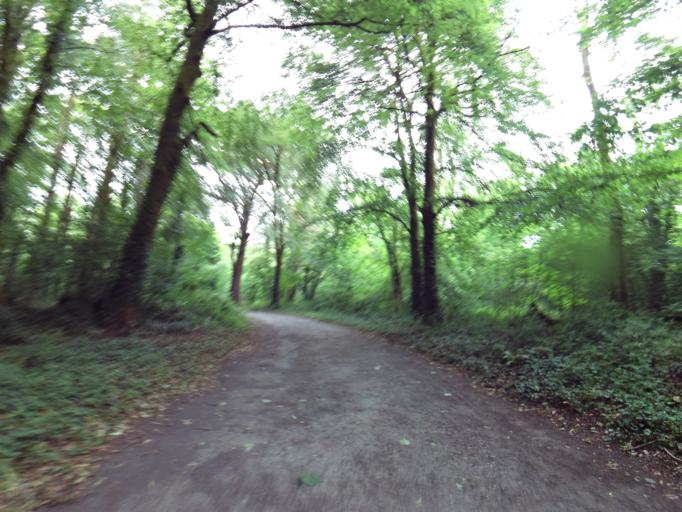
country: IE
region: Connaught
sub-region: County Galway
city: Gort
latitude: 53.0793
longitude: -8.8758
